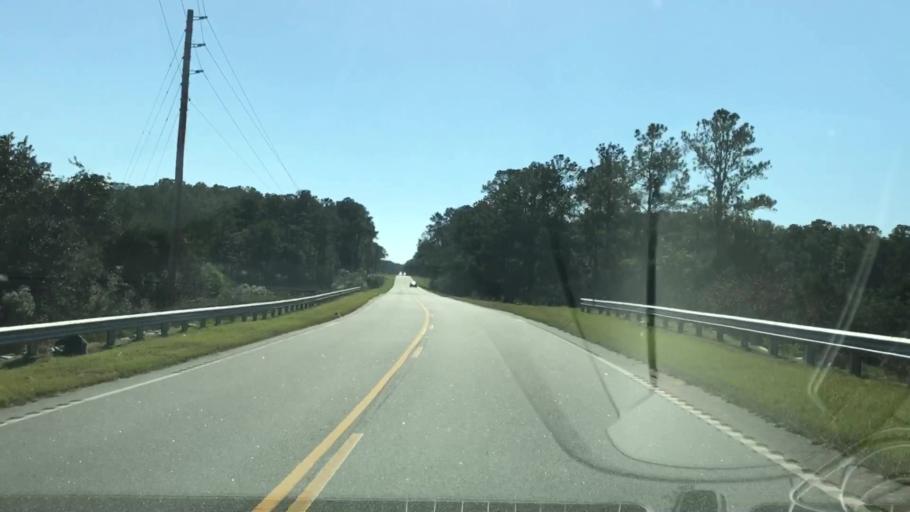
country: US
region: South Carolina
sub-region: Jasper County
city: Ridgeland
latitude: 32.4525
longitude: -80.8994
